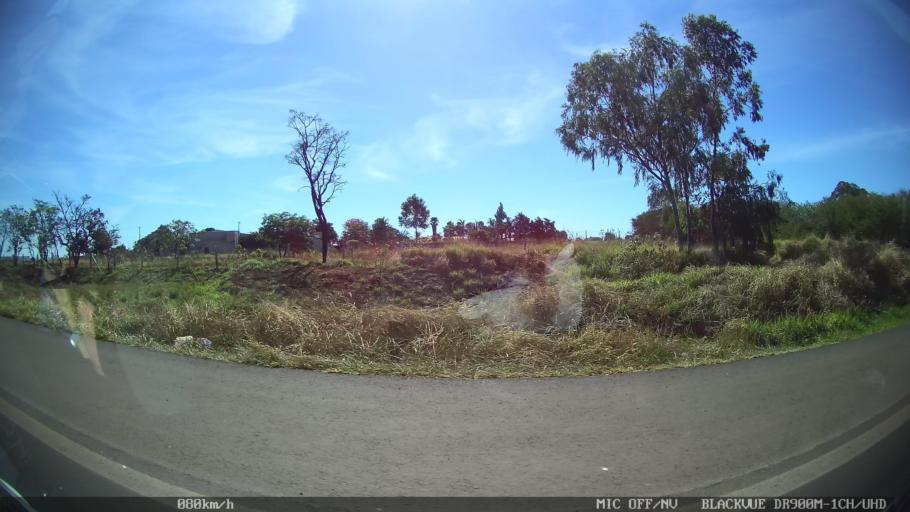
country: BR
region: Sao Paulo
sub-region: Franca
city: Franca
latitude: -20.5462
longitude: -47.4688
